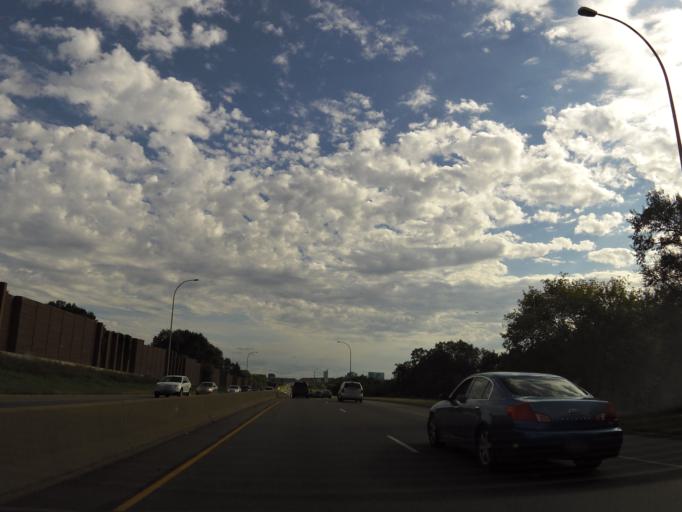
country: US
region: Minnesota
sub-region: Hennepin County
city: New Hope
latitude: 45.0014
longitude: -93.4010
